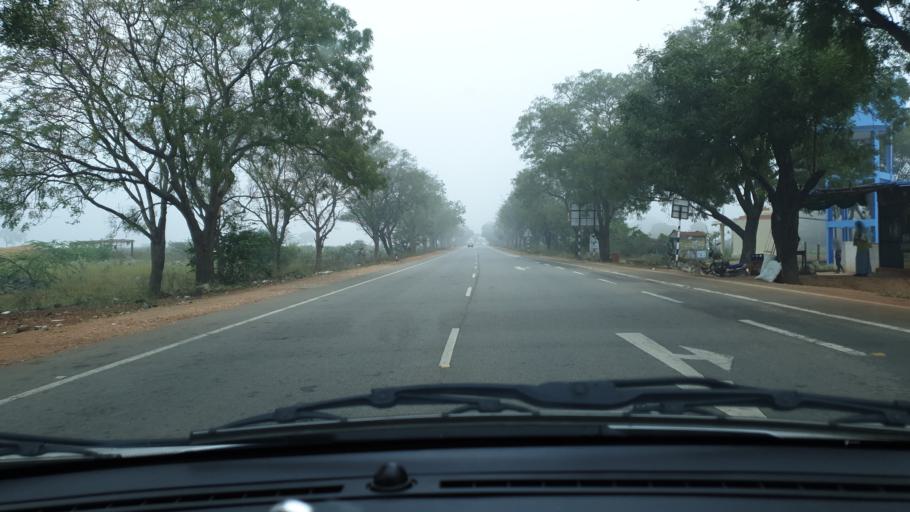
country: IN
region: Telangana
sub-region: Nalgonda
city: Devarkonda
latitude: 16.6308
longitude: 78.6124
